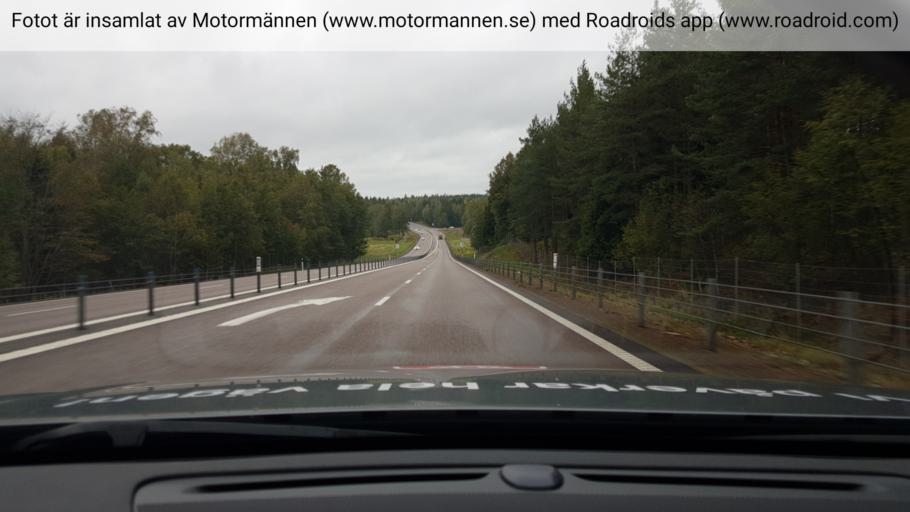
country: SE
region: Vaermland
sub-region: Kristinehamns Kommun
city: Kristinehamn
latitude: 59.3454
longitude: 14.0850
